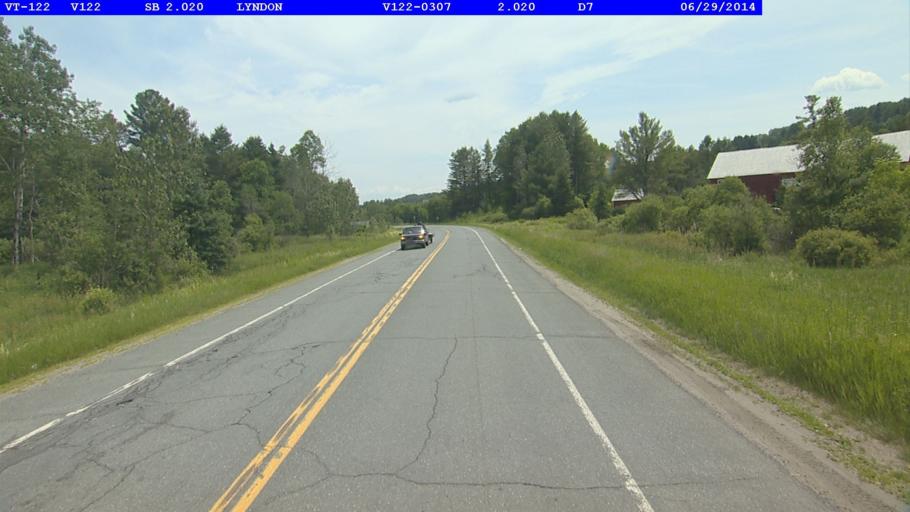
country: US
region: Vermont
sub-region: Caledonia County
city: Lyndonville
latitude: 44.5560
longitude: -72.0319
